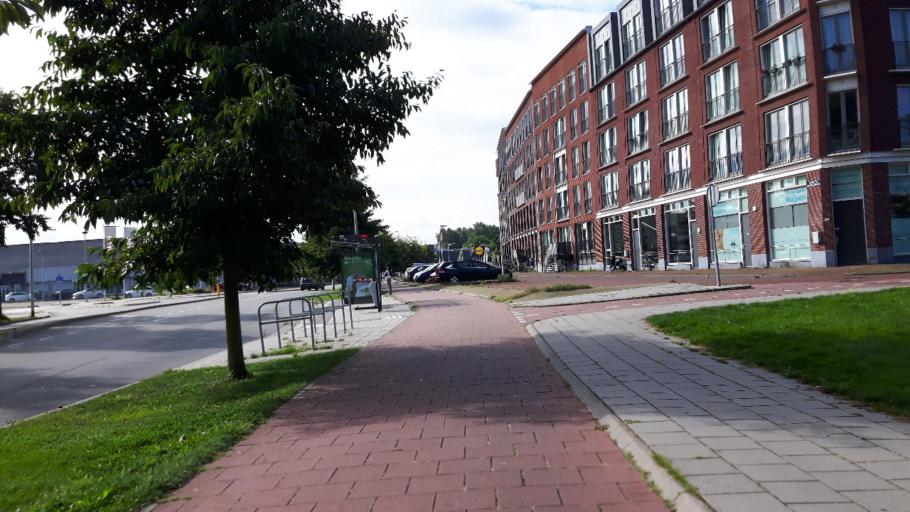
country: NL
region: North Holland
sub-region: Gemeente Purmerend
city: Purmerend
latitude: 52.5104
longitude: 4.9576
